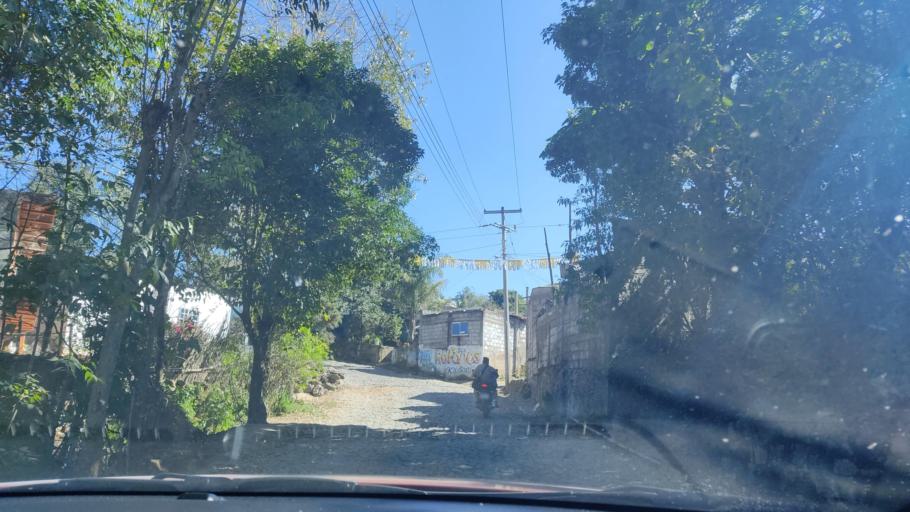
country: MX
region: Nayarit
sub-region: Jala
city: Rosa Blanca
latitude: 21.1019
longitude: -104.3423
